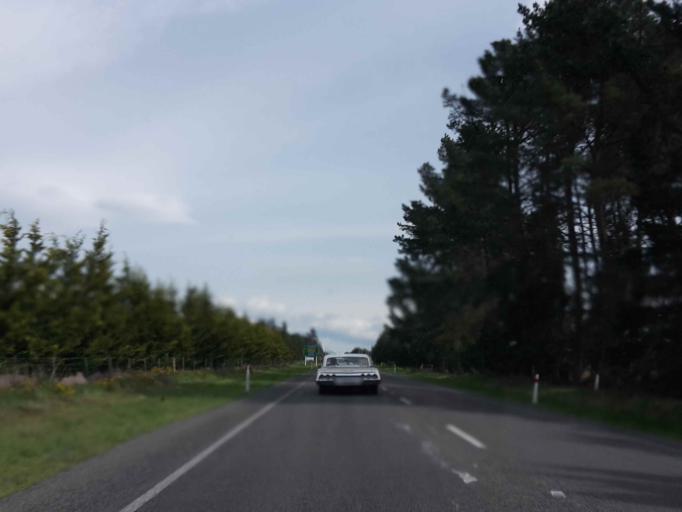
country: NZ
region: Canterbury
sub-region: Waimakariri District
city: Kaiapoi
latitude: -43.3806
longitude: 172.5396
